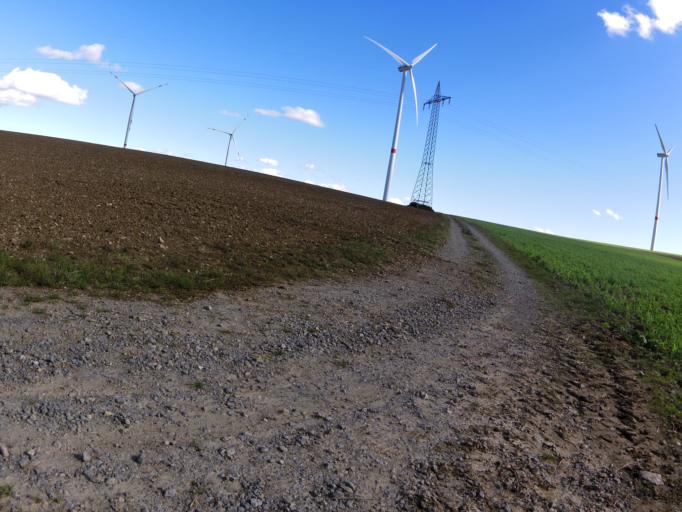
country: DE
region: Bavaria
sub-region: Regierungsbezirk Unterfranken
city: Hettstadt
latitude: 49.8314
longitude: 9.8201
